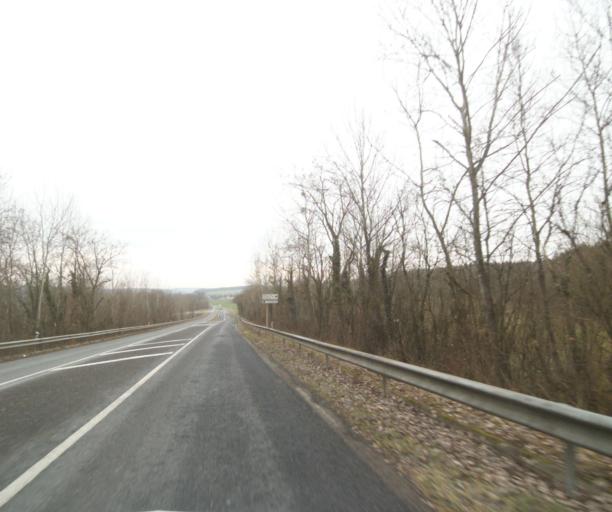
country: FR
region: Champagne-Ardenne
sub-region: Departement de la Haute-Marne
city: Bienville
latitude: 48.5693
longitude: 5.0377
